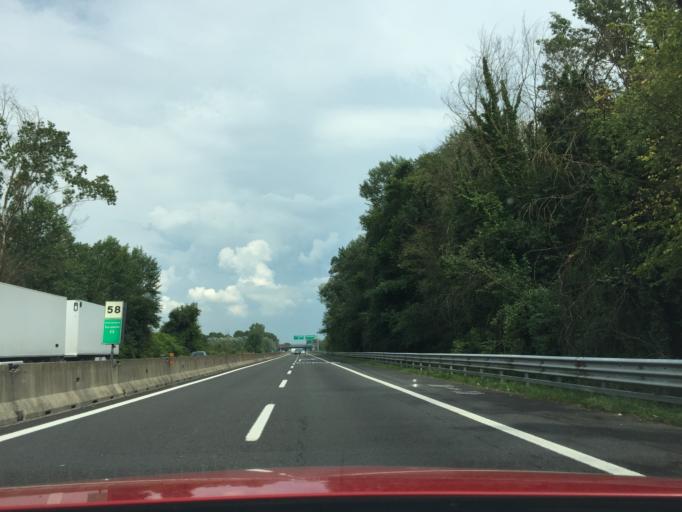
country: IT
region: Tuscany
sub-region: Provincia di Lucca
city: Capannori
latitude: 43.8238
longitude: 10.5856
